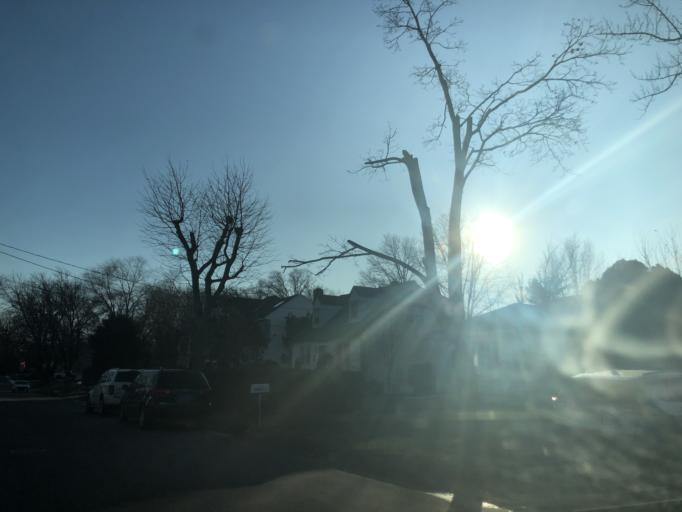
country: US
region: New Jersey
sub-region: Middlesex County
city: Fords
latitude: 40.5448
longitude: -74.3066
